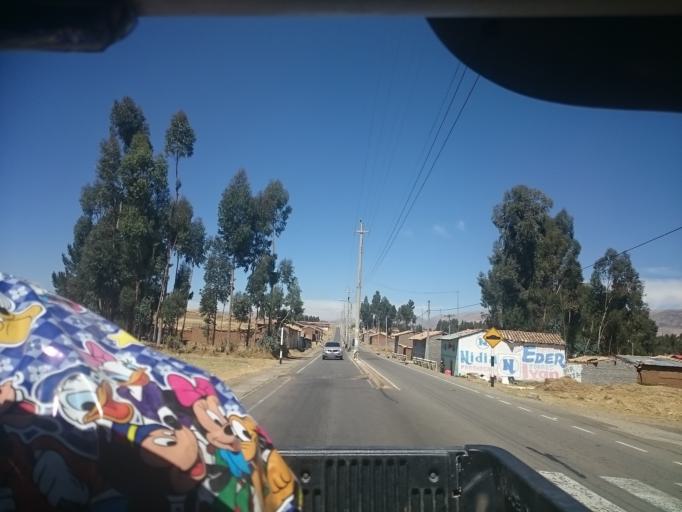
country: PE
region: Junin
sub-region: Provincia de Jauja
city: Acolla
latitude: -11.7183
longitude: -75.5517
